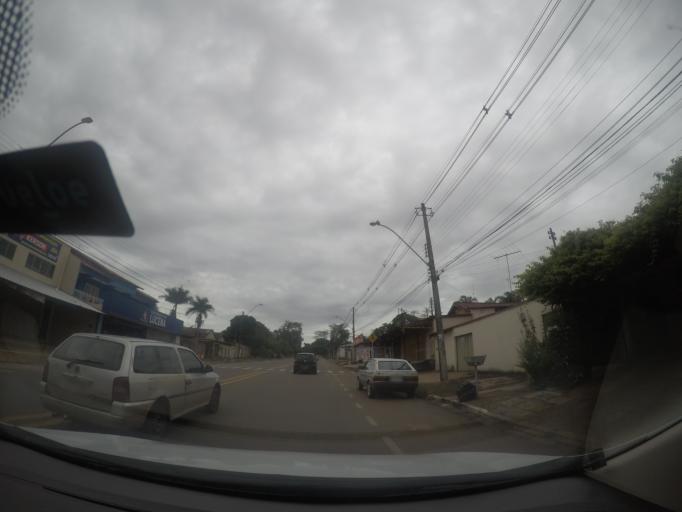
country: BR
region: Goias
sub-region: Goiania
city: Goiania
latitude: -16.6074
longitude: -49.2949
